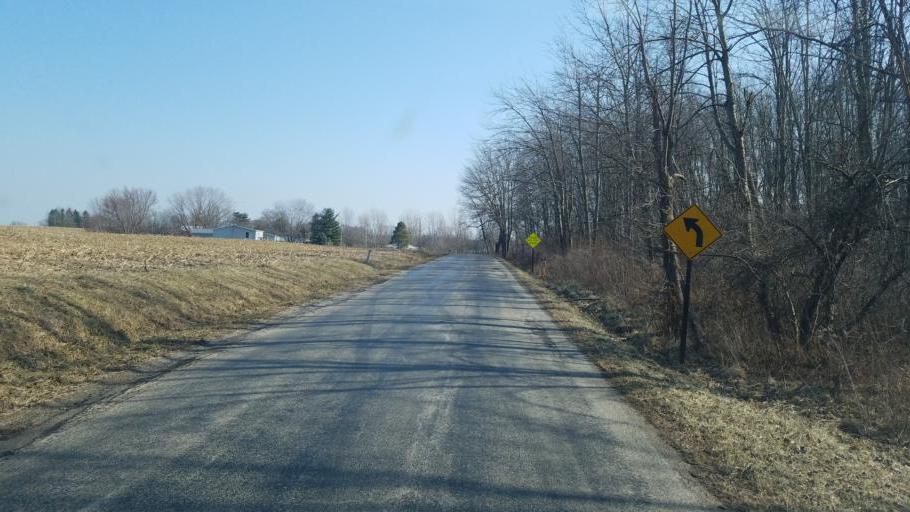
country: US
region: Ohio
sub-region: Richland County
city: Lincoln Heights
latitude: 40.8477
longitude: -82.5212
